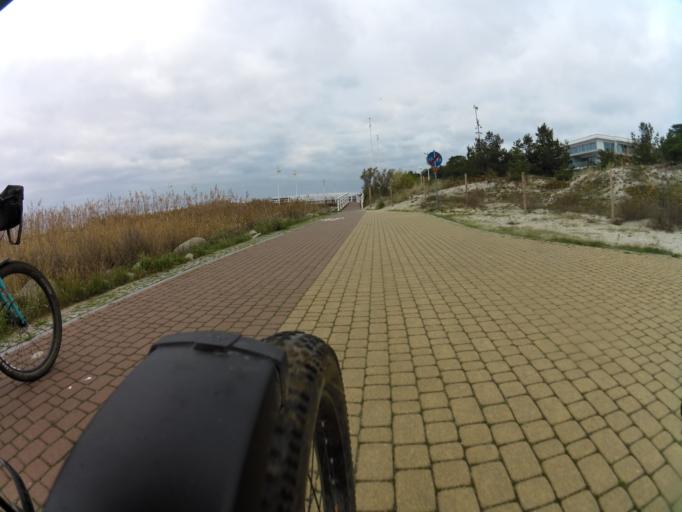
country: PL
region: Pomeranian Voivodeship
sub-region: Powiat pucki
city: Jastarnia
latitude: 54.6815
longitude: 18.7112
